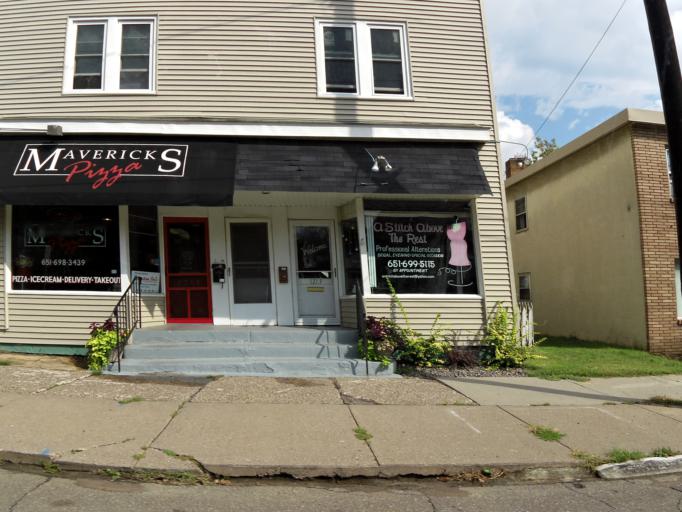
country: US
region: Minnesota
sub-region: Dakota County
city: Mendota Heights
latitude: 44.9270
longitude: -93.1513
